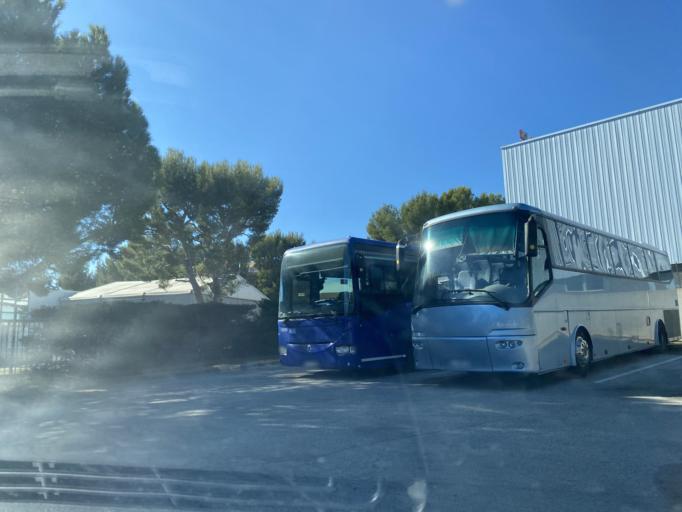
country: FR
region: Provence-Alpes-Cote d'Azur
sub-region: Departement des Bouches-du-Rhone
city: Ceyreste
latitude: 43.2055
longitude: 5.6033
